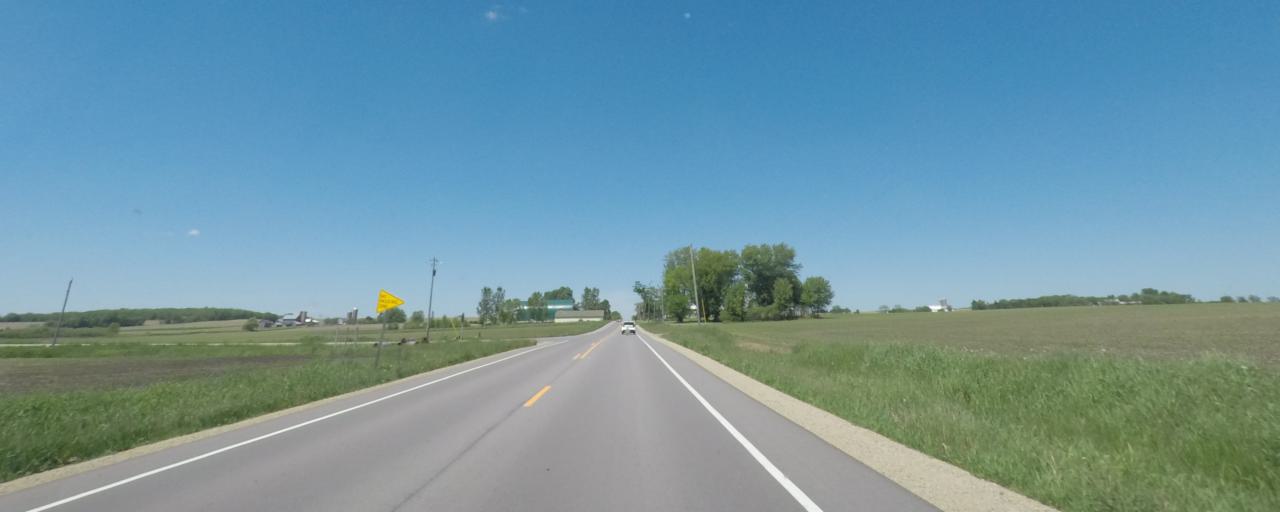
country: US
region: Wisconsin
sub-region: Green County
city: Brooklyn
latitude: 42.8129
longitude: -89.3692
